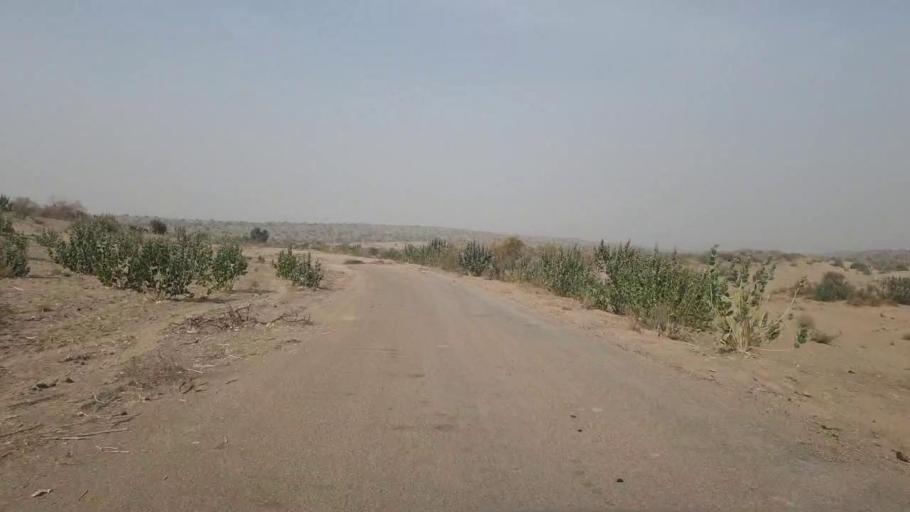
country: PK
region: Sindh
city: Chor
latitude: 25.6330
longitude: 69.9306
